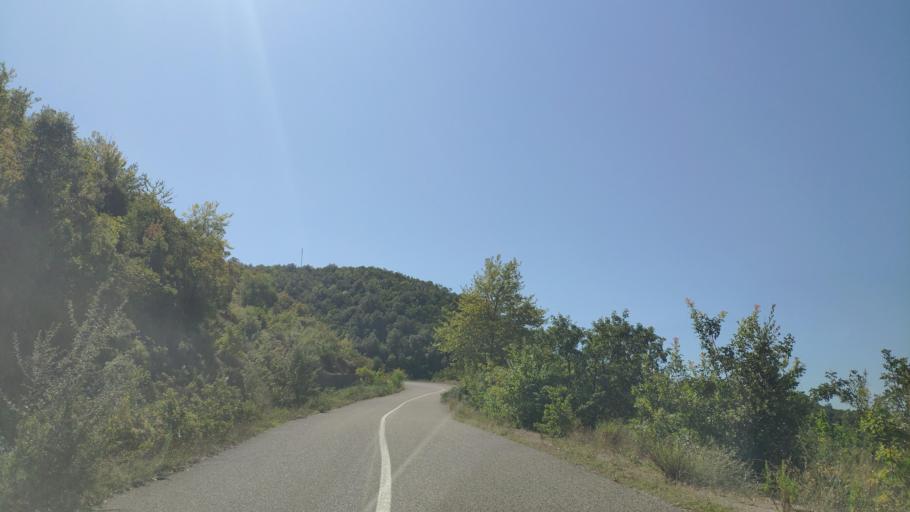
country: GR
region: Central Greece
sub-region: Nomos Evrytanias
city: Kerasochori
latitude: 39.0067
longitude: 21.5346
